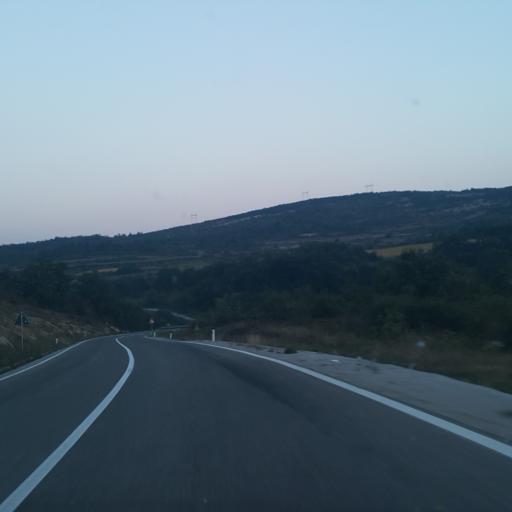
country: RS
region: Central Serbia
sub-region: Nisavski Okrug
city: Svrljig
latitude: 43.4527
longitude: 22.1798
